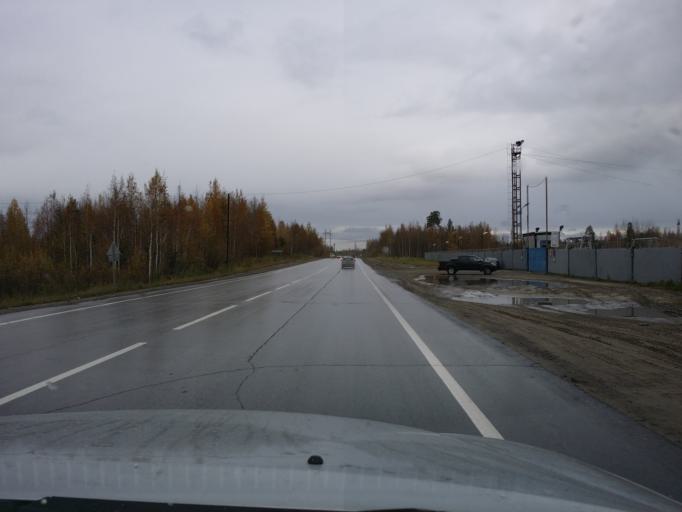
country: RU
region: Khanty-Mansiyskiy Avtonomnyy Okrug
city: Megion
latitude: 61.0752
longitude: 76.1166
